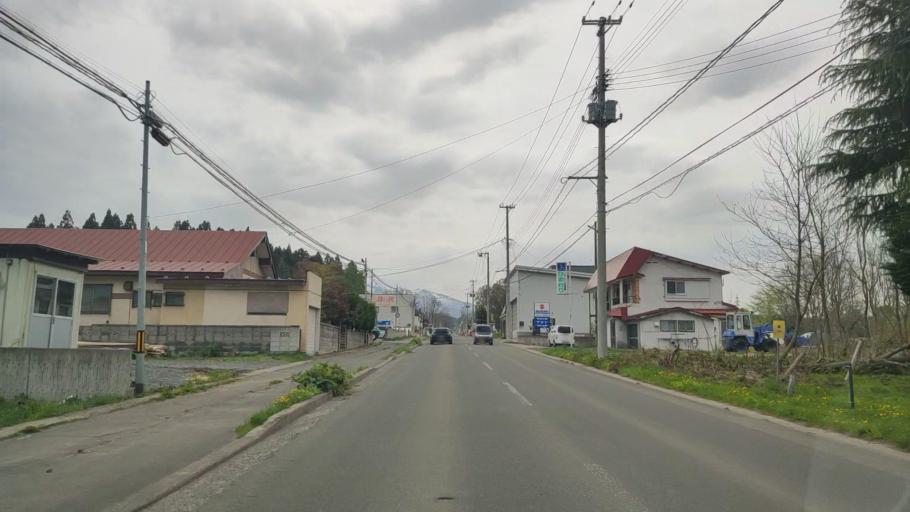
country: JP
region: Aomori
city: Aomori Shi
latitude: 40.7822
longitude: 140.7916
